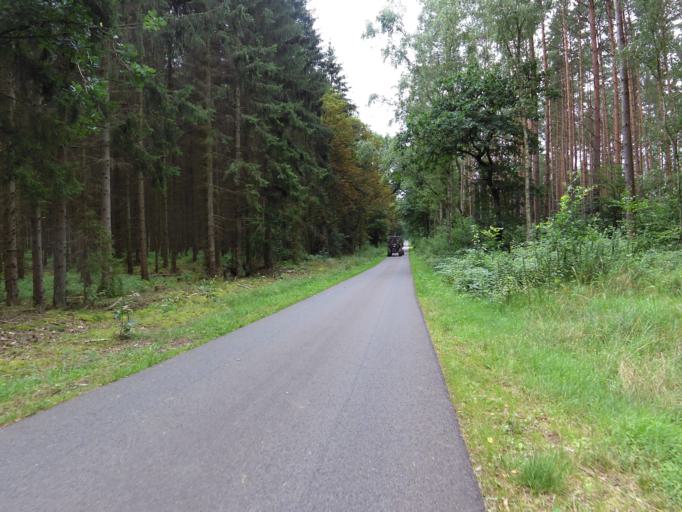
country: DE
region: Brandenburg
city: Templin
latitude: 53.1549
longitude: 13.4364
